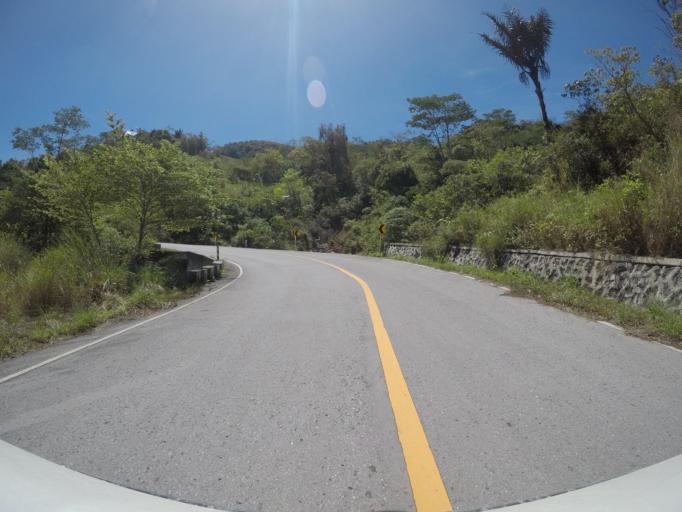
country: TL
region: Manatuto
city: Manatuto
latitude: -8.7676
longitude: 125.9672
